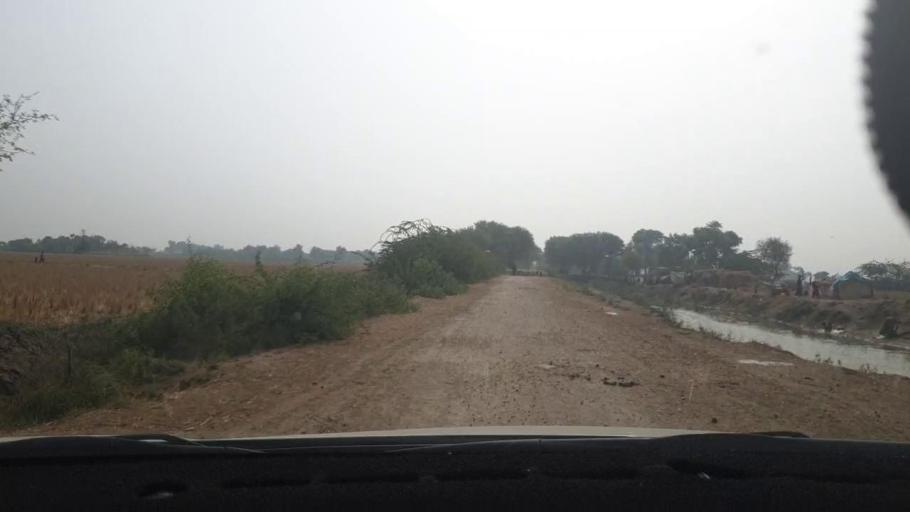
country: PK
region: Sindh
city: Tando Muhammad Khan
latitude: 25.0646
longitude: 68.5071
